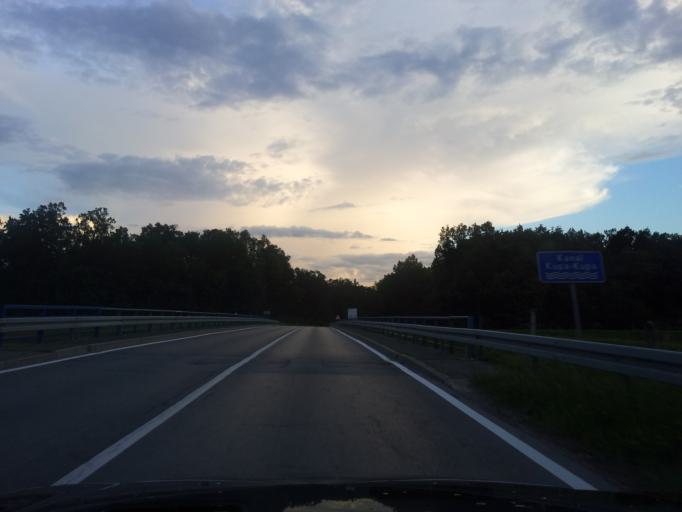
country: HR
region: Karlovacka
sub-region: Grad Karlovac
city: Karlovac
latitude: 45.5432
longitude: 15.5698
